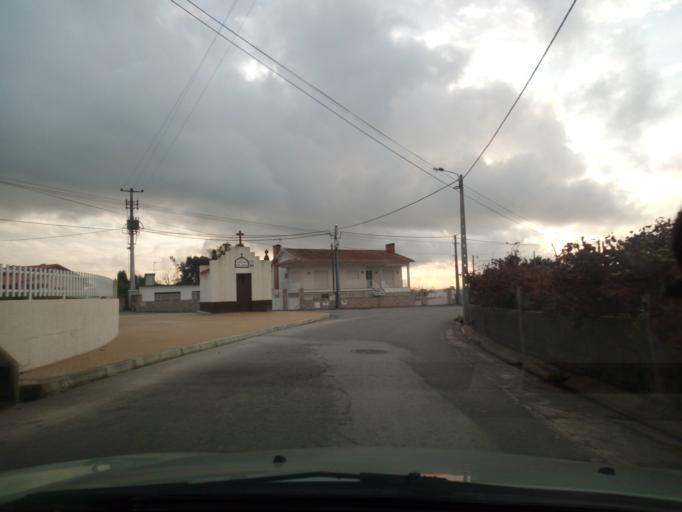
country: PT
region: Aveiro
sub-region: Oliveira do Bairro
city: Oliveira do Bairro
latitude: 40.5490
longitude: -8.4819
